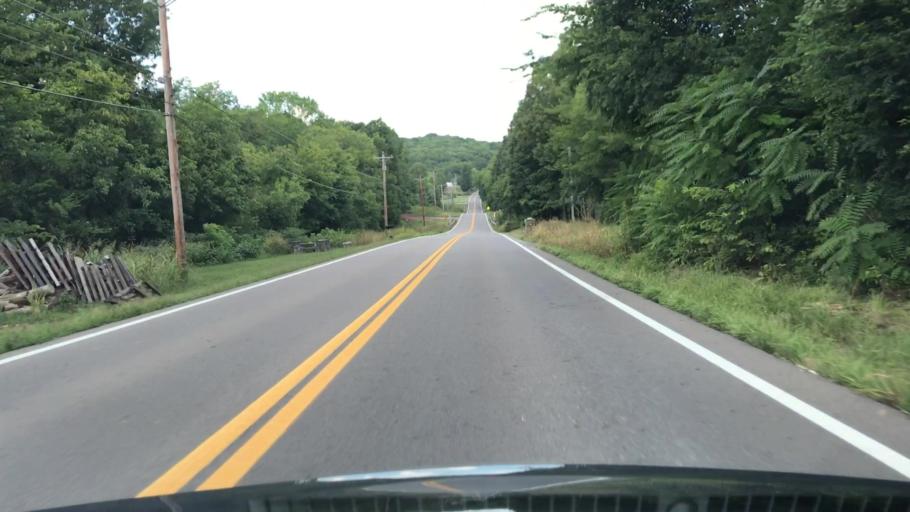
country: US
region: Tennessee
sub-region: Williamson County
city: Nolensville
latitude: 35.8508
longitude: -86.5896
